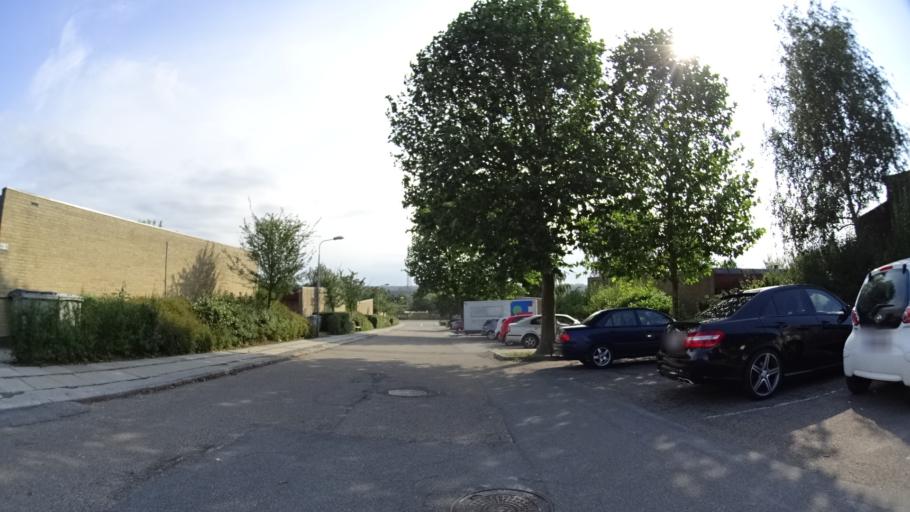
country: DK
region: Central Jutland
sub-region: Arhus Kommune
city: Stavtrup
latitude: 56.1550
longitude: 10.1146
